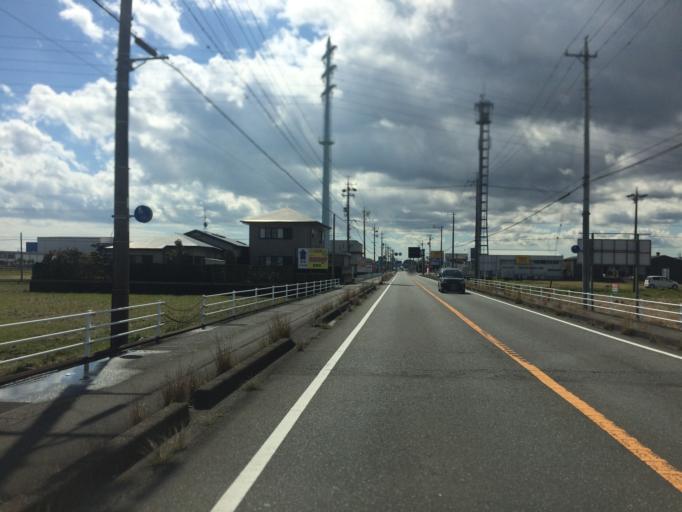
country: JP
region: Shizuoka
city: Fujieda
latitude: 34.8086
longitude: 138.2705
